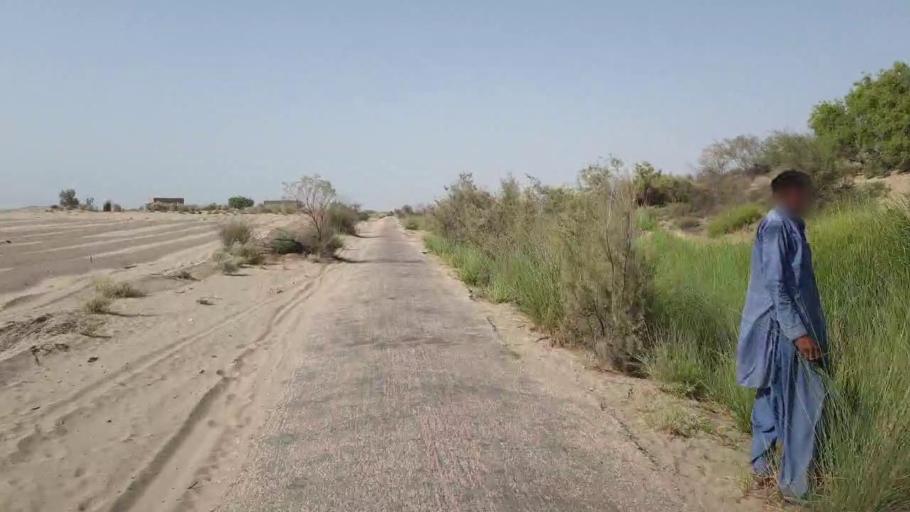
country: PK
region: Sindh
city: Jam Sahib
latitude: 26.5984
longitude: 68.9240
